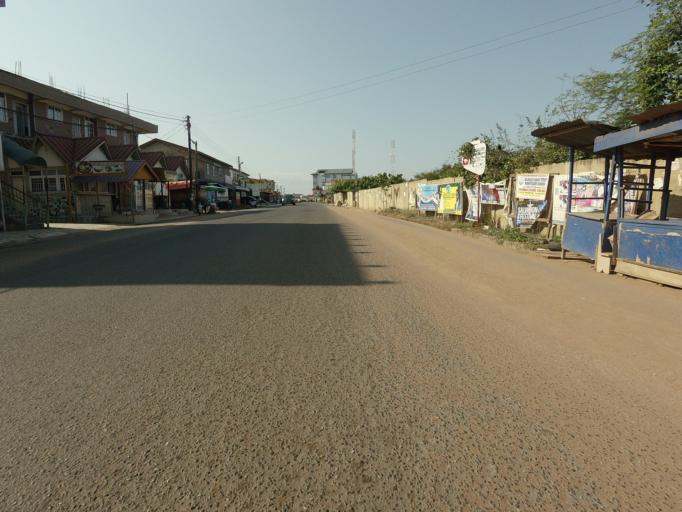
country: GH
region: Greater Accra
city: Nungua
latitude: 5.6268
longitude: -0.0904
